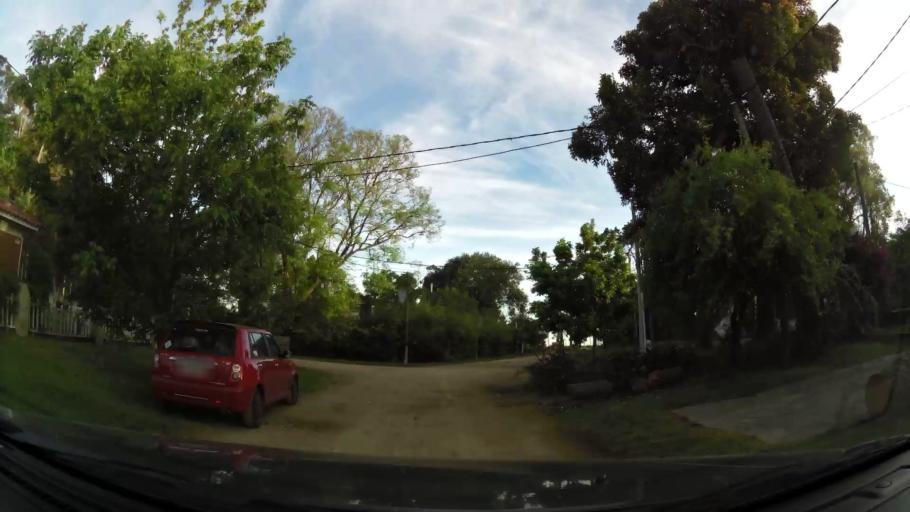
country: UY
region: Canelones
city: Atlantida
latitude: -34.7722
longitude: -55.8060
